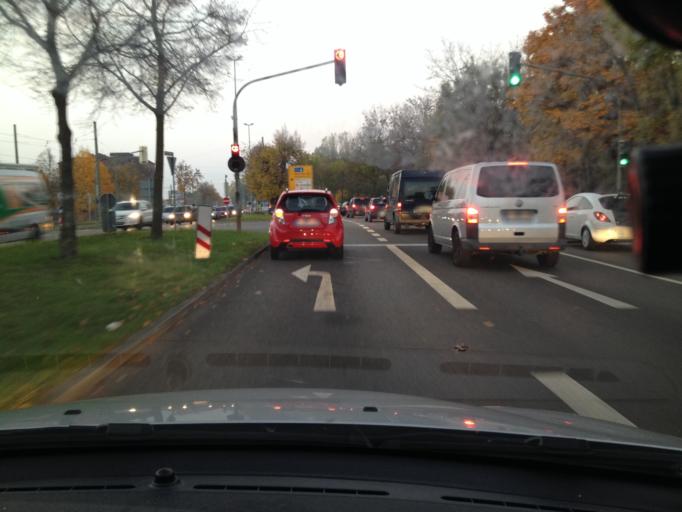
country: DE
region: Bavaria
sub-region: Swabia
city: Augsburg
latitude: 48.3371
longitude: 10.9079
